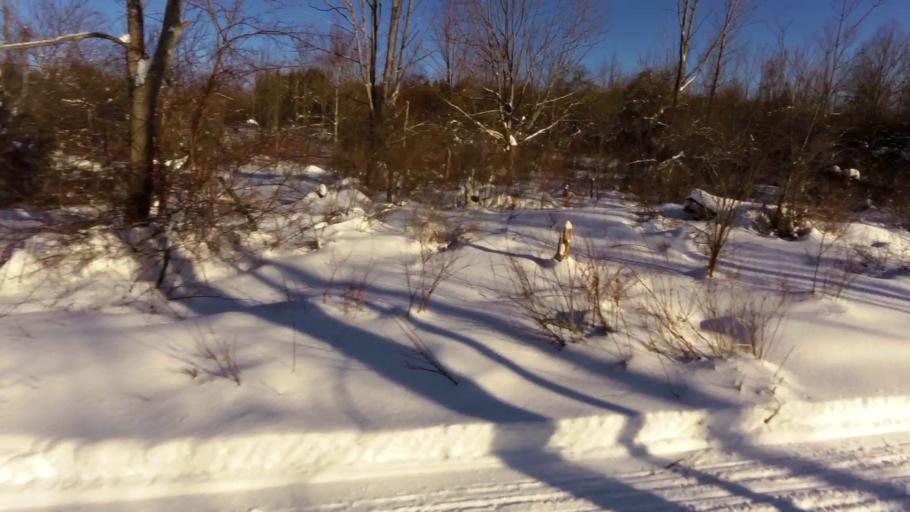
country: US
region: New York
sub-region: Chautauqua County
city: Mayville
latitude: 42.2485
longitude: -79.3917
